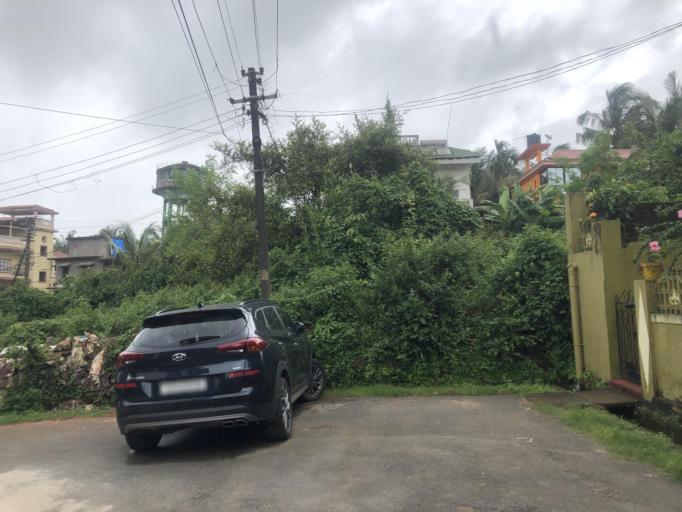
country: IN
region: Goa
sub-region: North Goa
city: Serula
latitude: 15.5481
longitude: 73.8275
